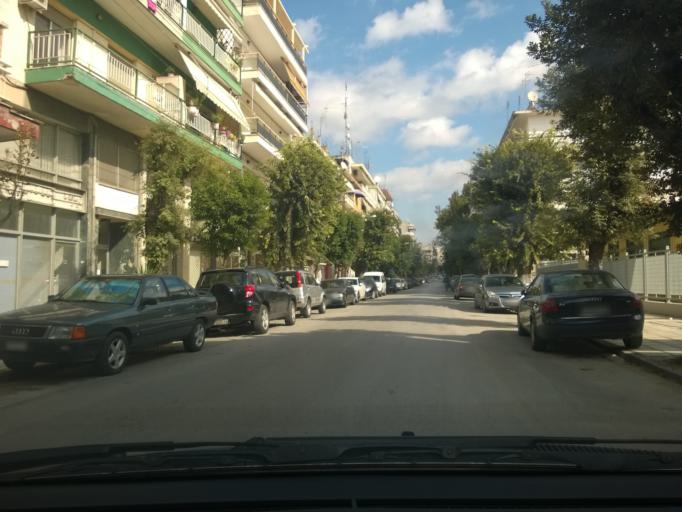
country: GR
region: Central Macedonia
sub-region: Nomos Thessalonikis
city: Ampelokipoi
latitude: 40.6502
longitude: 22.9262
